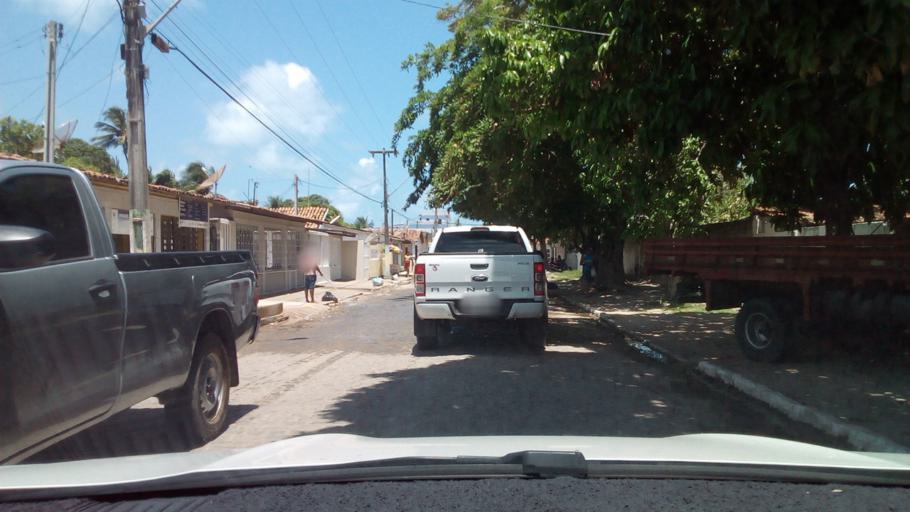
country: BR
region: Paraiba
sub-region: Pitimbu
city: Pitimbu
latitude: -7.4783
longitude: -34.8119
